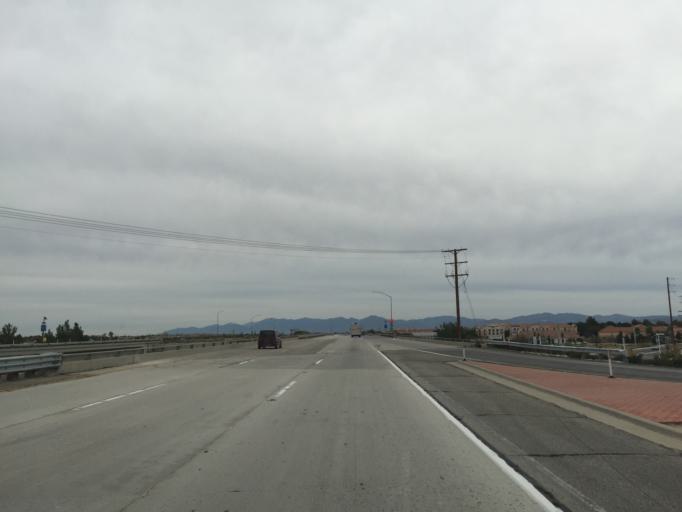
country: US
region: California
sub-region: Los Angeles County
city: Lancaster
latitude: 34.6838
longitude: -118.1662
